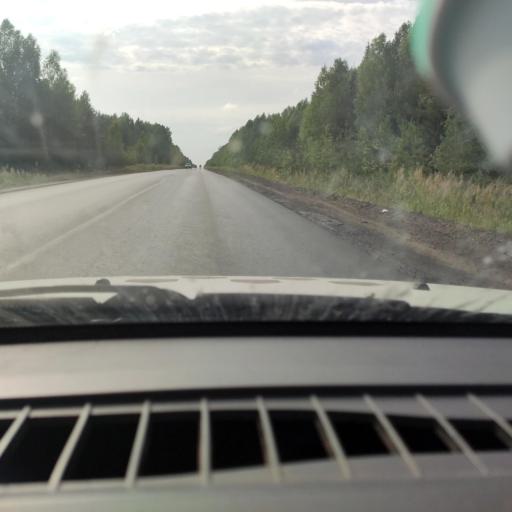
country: RU
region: Kirov
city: Chernaya Kholunitsa
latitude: 58.8809
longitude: 51.4370
